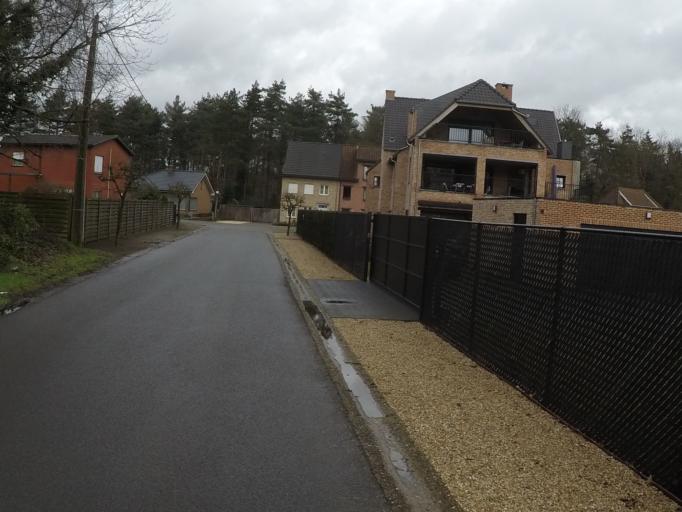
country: BE
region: Flanders
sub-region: Provincie Antwerpen
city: Zandhoven
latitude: 51.2161
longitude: 4.6560
